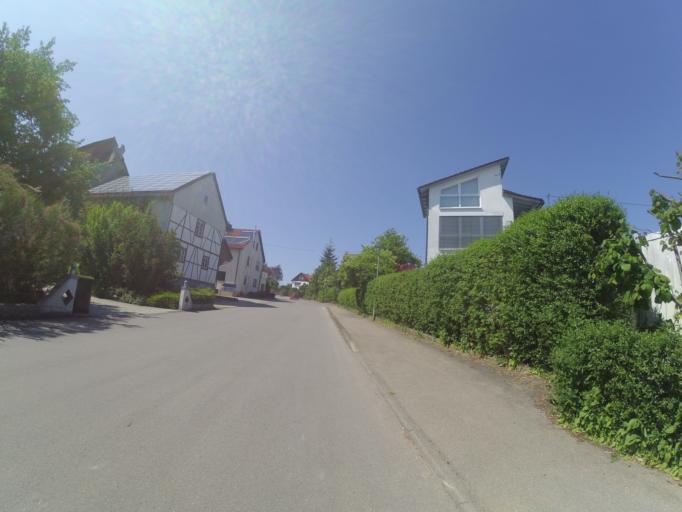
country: DE
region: Baden-Wuerttemberg
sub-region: Tuebingen Region
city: Merklingen
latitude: 48.5071
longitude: 9.7561
